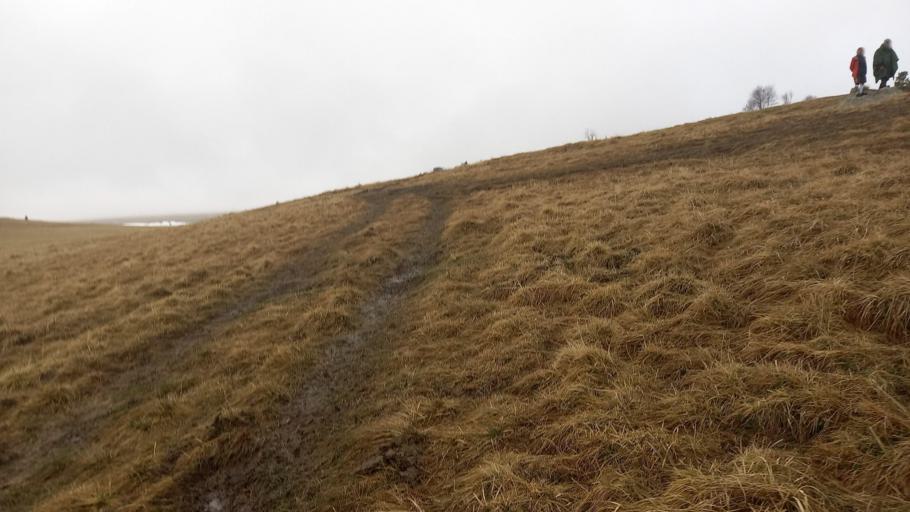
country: RU
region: Kabardino-Balkariya
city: Terskol
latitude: 43.5211
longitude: 42.4251
